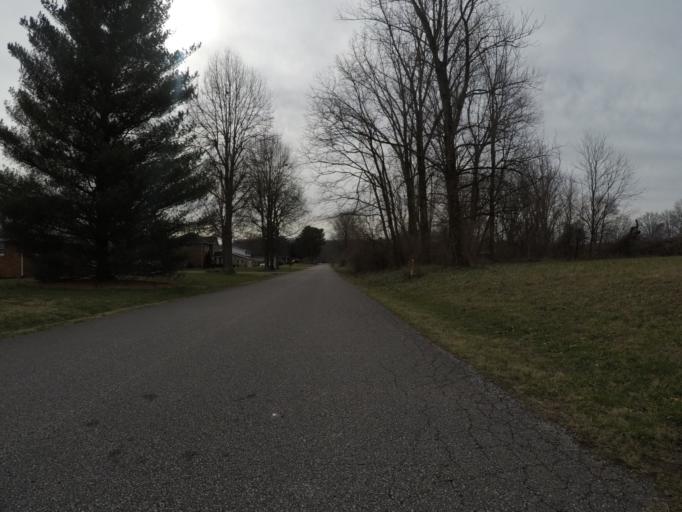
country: US
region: West Virginia
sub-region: Cabell County
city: Pea Ridge
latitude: 38.4494
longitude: -82.3504
